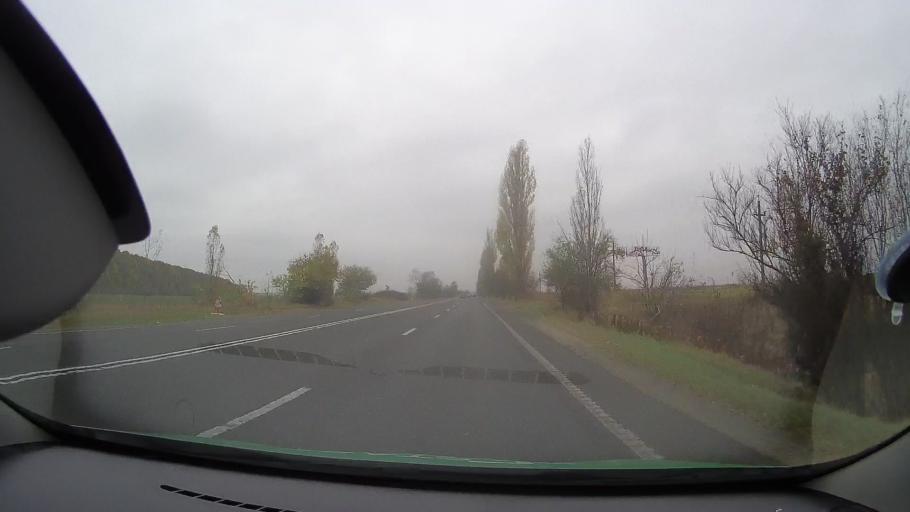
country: RO
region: Prahova
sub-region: Comuna Gorgota
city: Potigrafu
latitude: 44.7626
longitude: 26.1042
